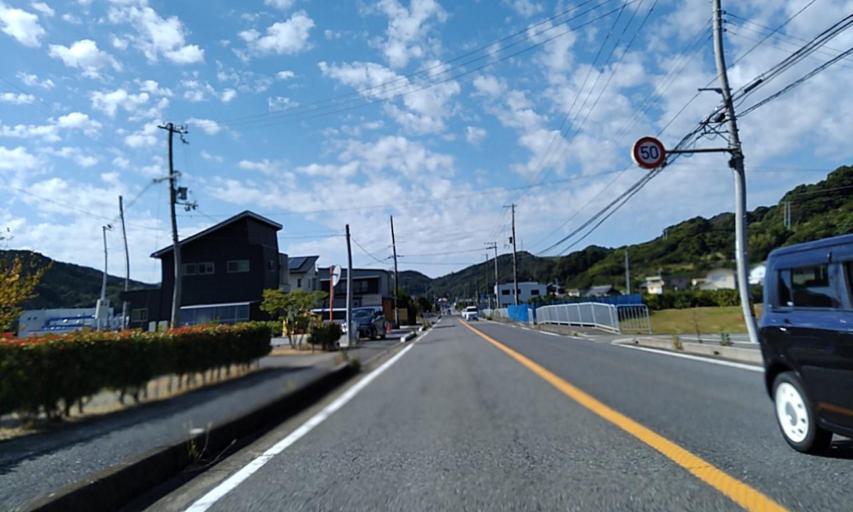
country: JP
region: Wakayama
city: Gobo
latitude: 33.9740
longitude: 135.1386
